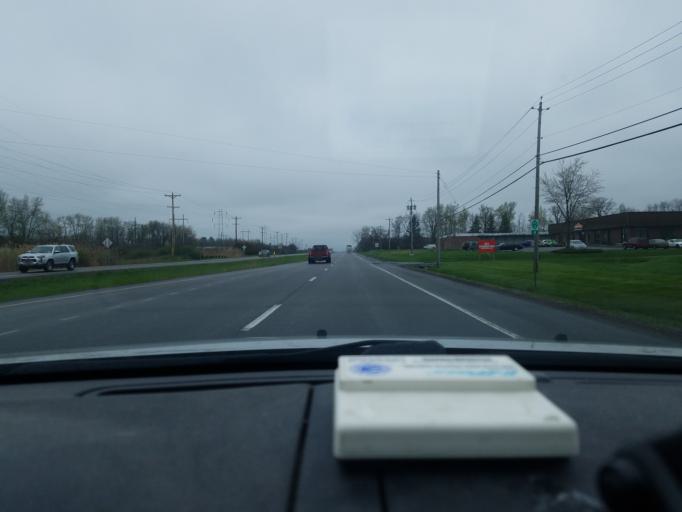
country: US
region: New York
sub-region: Onondaga County
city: East Syracuse
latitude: 43.1025
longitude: -76.0766
